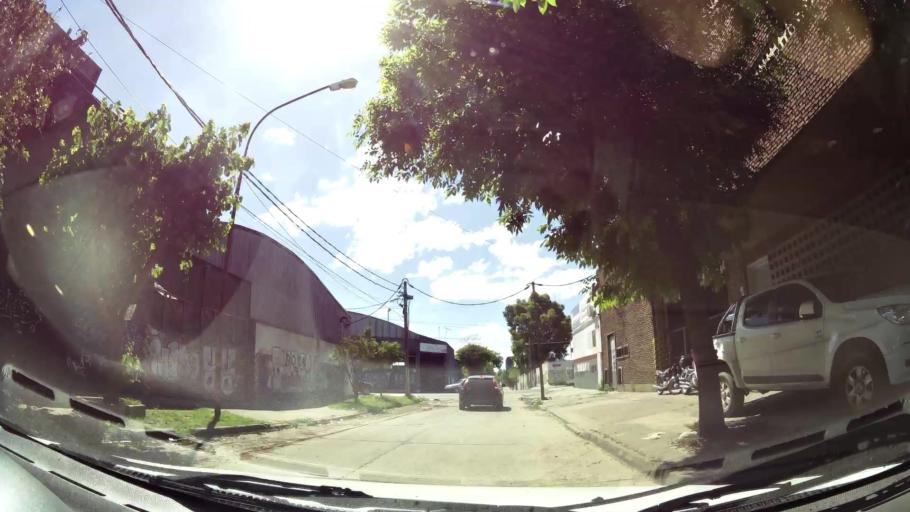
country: AR
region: Buenos Aires
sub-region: Partido de General San Martin
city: General San Martin
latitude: -34.5216
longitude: -58.5701
